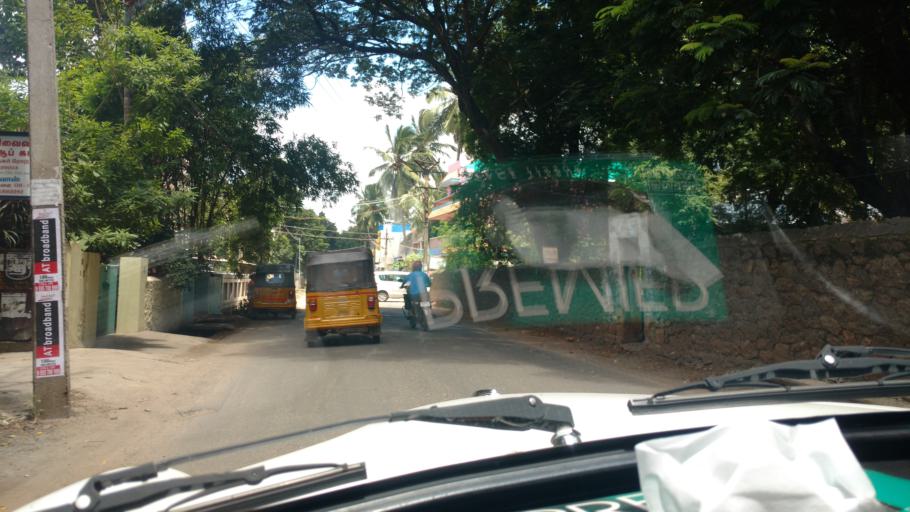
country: IN
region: Tamil Nadu
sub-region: Kanniyakumari
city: Nagercoil
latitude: 8.1828
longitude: 77.4161
